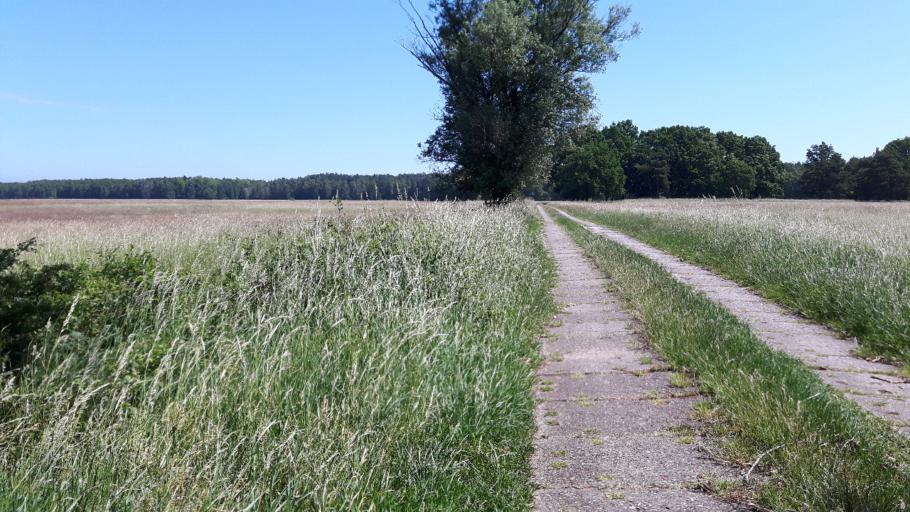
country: PL
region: Pomeranian Voivodeship
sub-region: Powiat slupski
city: Smoldzino
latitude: 54.6692
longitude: 17.1631
